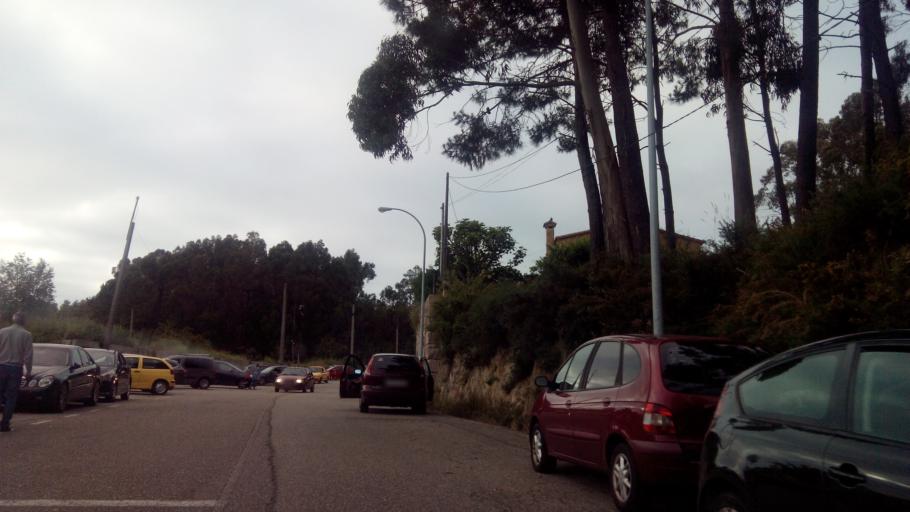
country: ES
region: Galicia
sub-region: Provincia de Pontevedra
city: Nigran
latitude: 42.1198
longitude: -8.8009
